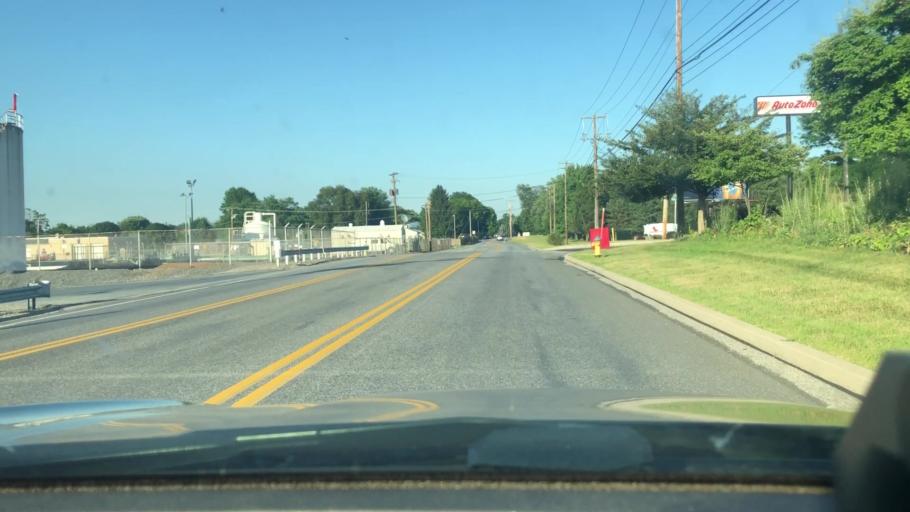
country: US
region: Pennsylvania
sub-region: Cumberland County
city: Shiremanstown
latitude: 40.2201
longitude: -76.9695
